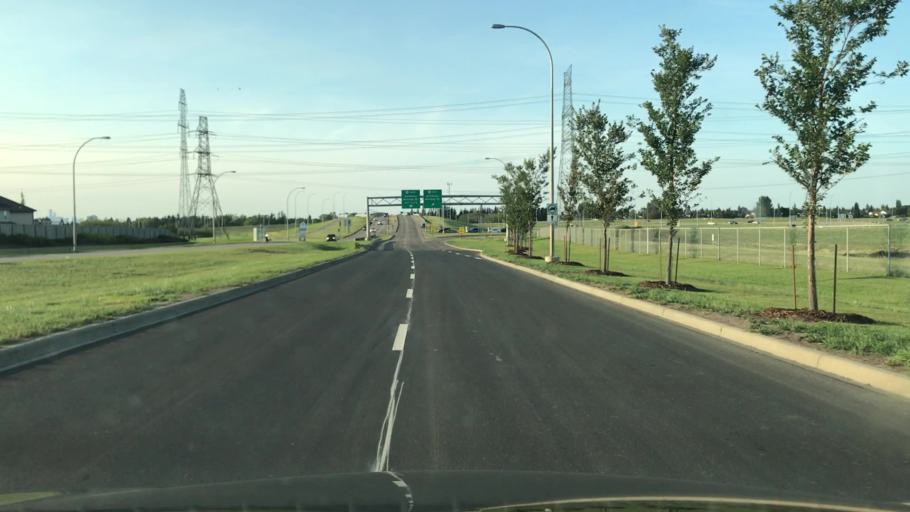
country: CA
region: Alberta
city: Beaumont
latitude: 53.4307
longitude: -113.4177
